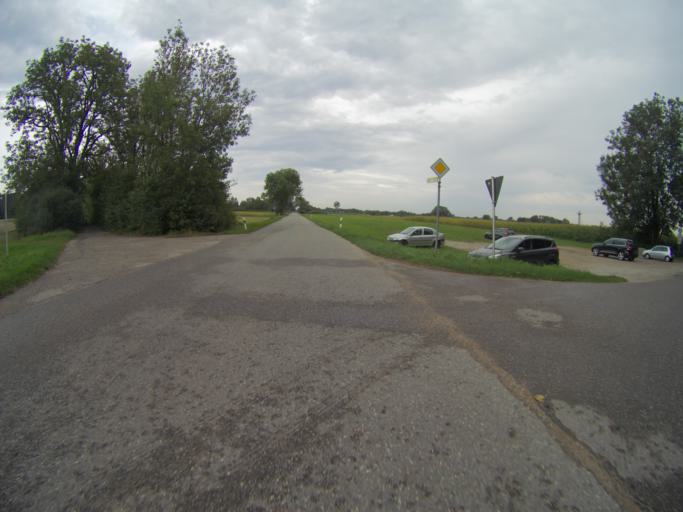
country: DE
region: Bavaria
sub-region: Upper Bavaria
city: Marzling
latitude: 48.3887
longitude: 11.7937
